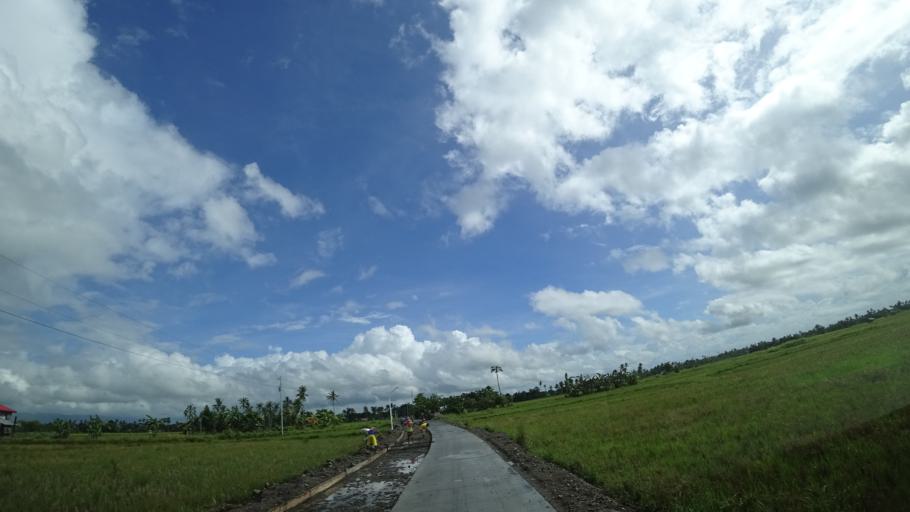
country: PH
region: Eastern Visayas
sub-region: Province of Leyte
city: Cabacungan
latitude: 10.9100
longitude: 124.9777
